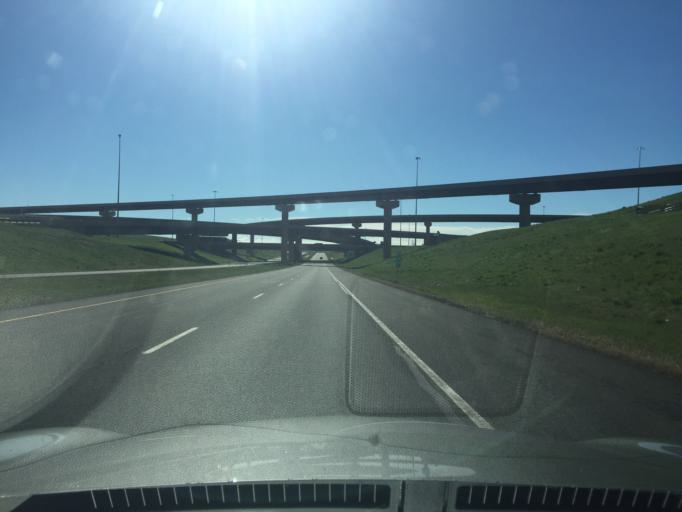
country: US
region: Colorado
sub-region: Boulder County
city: Erie
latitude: 39.9823
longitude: -104.9919
